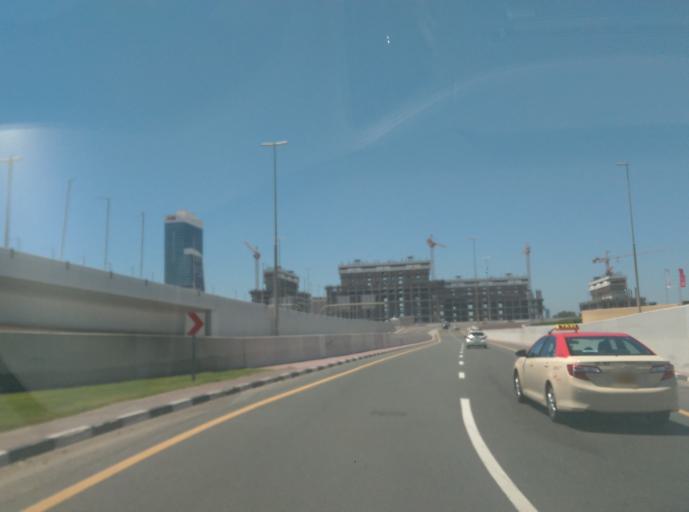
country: AE
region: Dubai
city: Dubai
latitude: 25.0956
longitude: 55.1641
